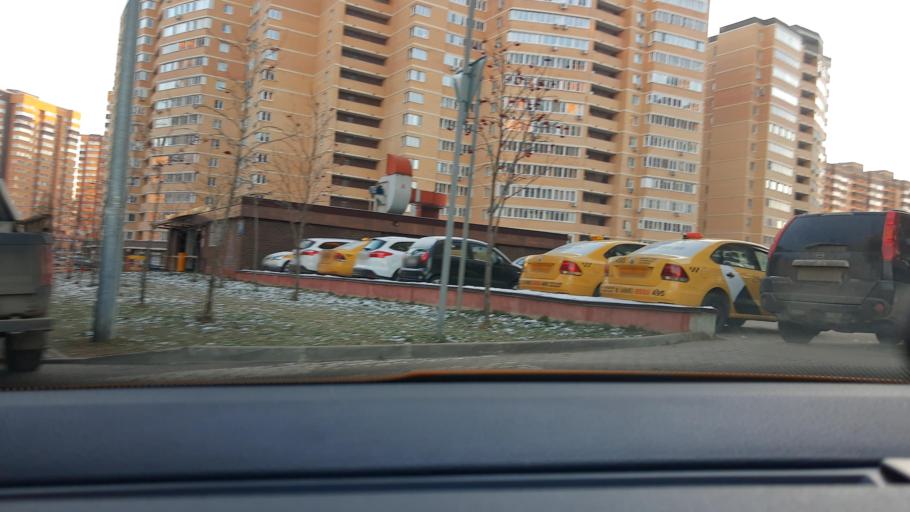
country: RU
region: Moskovskaya
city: Dolgoprudnyy
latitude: 55.9640
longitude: 37.5254
